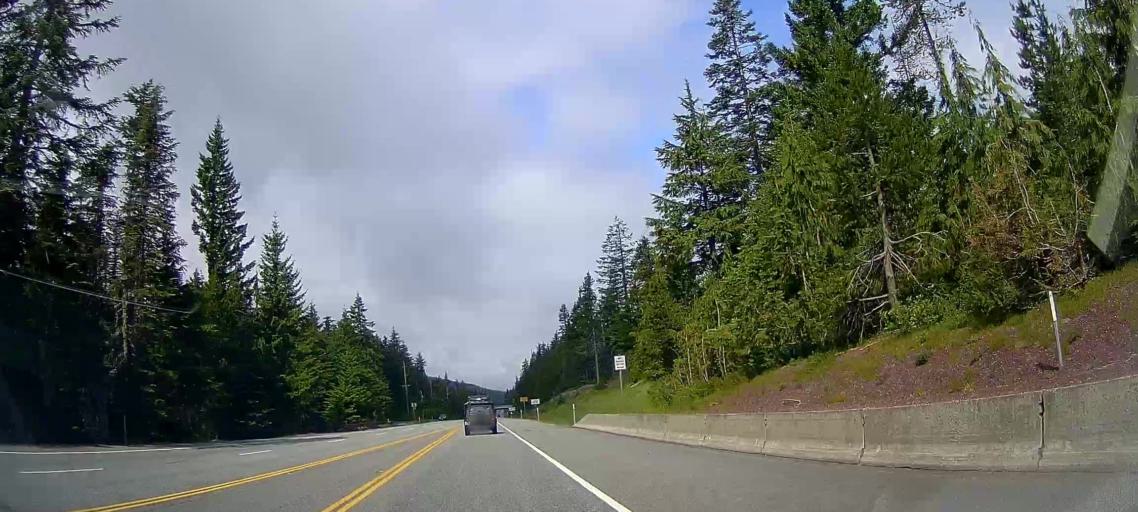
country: US
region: Oregon
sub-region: Clackamas County
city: Mount Hood Village
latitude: 45.3022
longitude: -121.7491
